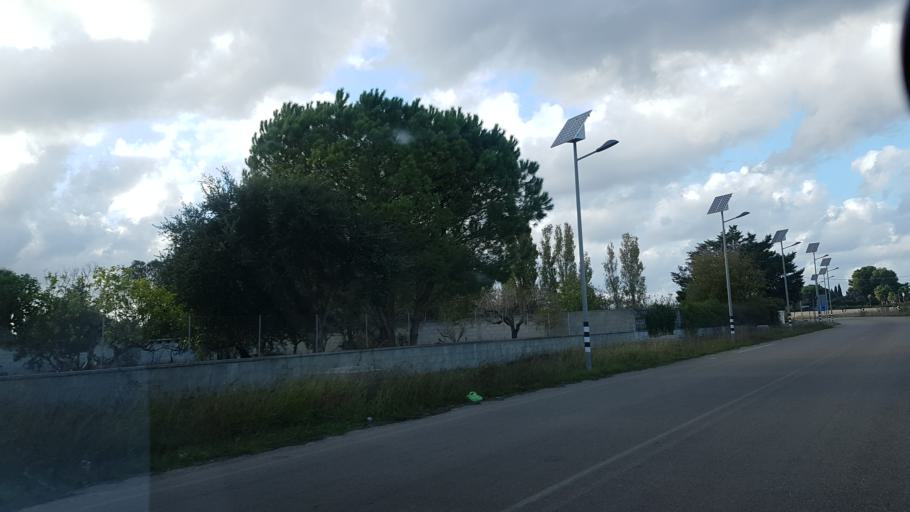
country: IT
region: Apulia
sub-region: Provincia di Brindisi
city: San Pietro Vernotico
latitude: 40.4972
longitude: 18.0064
